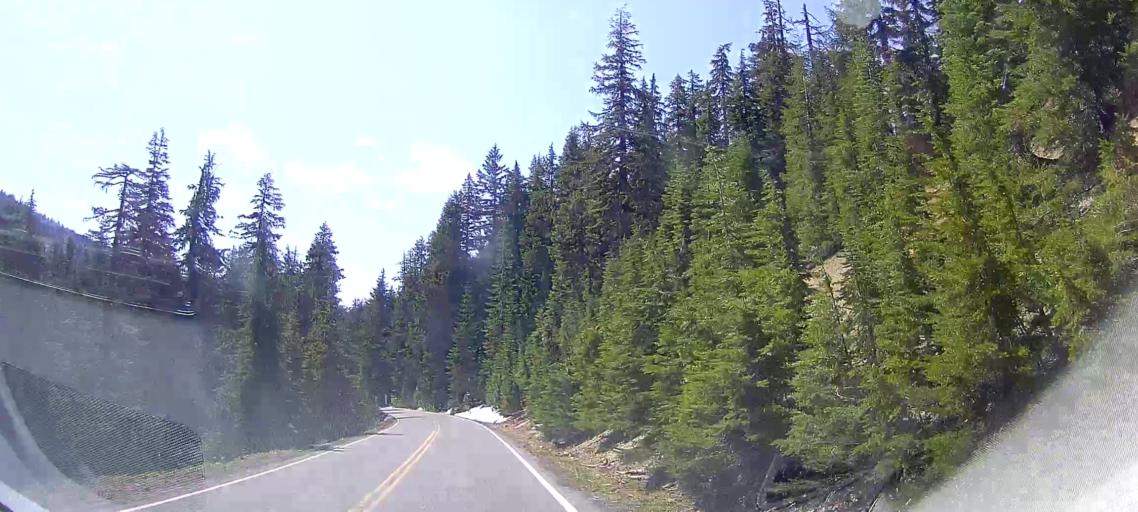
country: US
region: Oregon
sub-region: Klamath County
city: Klamath Falls
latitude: 42.8939
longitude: -122.0994
